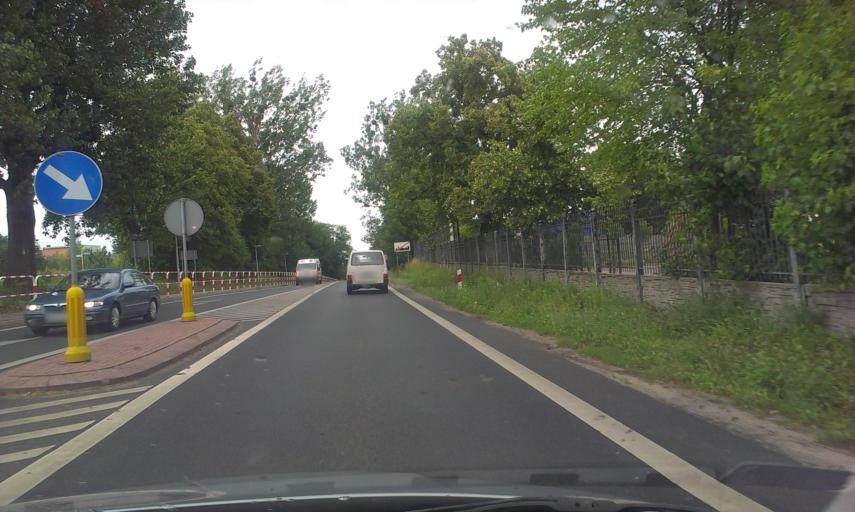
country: PL
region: Greater Poland Voivodeship
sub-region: Powiat obornicki
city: Oborniki
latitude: 52.6302
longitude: 16.8088
